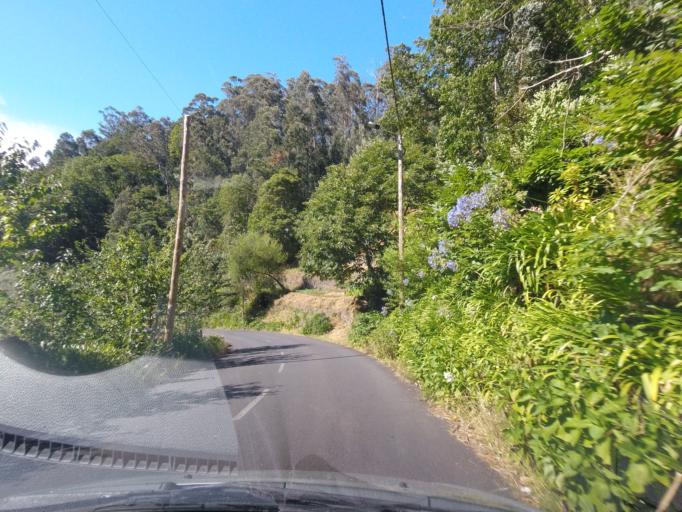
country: PT
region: Madeira
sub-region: Santa Cruz
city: Camacha
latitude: 32.6912
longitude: -16.8511
